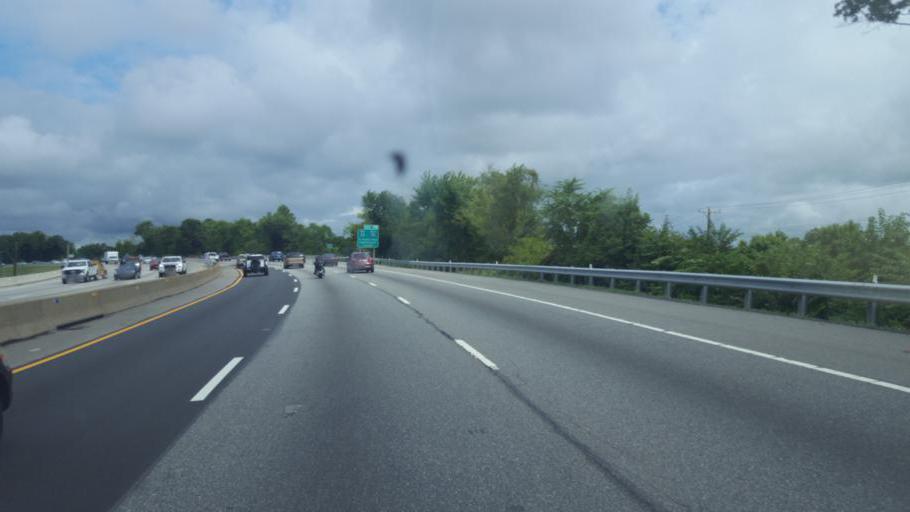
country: US
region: Virginia
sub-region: City of Richmond
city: Richmond
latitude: 37.5689
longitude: -77.4534
